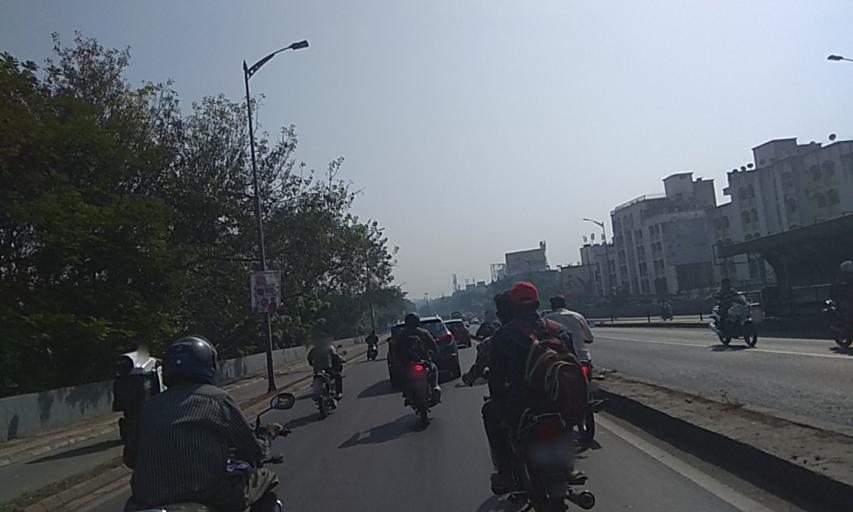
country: IN
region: Maharashtra
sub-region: Pune Division
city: Pune
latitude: 18.5051
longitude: 73.9178
